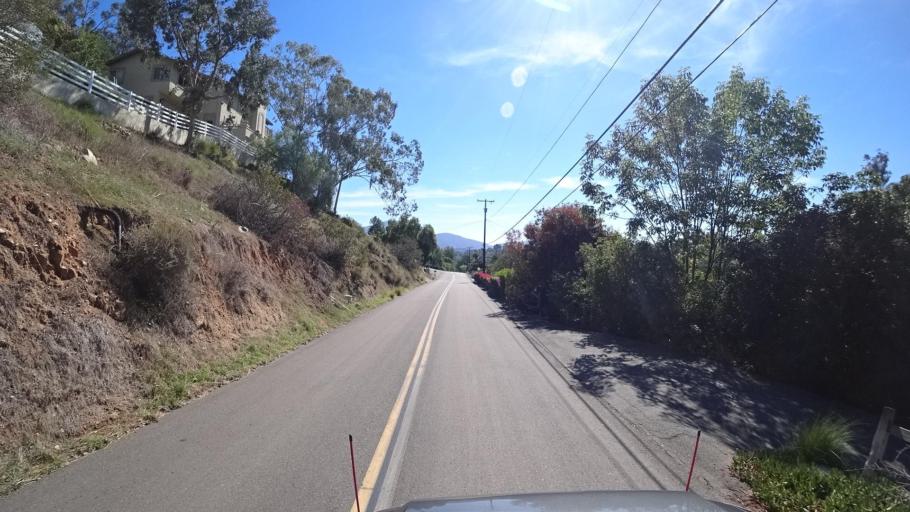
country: US
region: California
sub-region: San Diego County
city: Casa de Oro-Mount Helix
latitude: 32.7592
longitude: -116.9694
